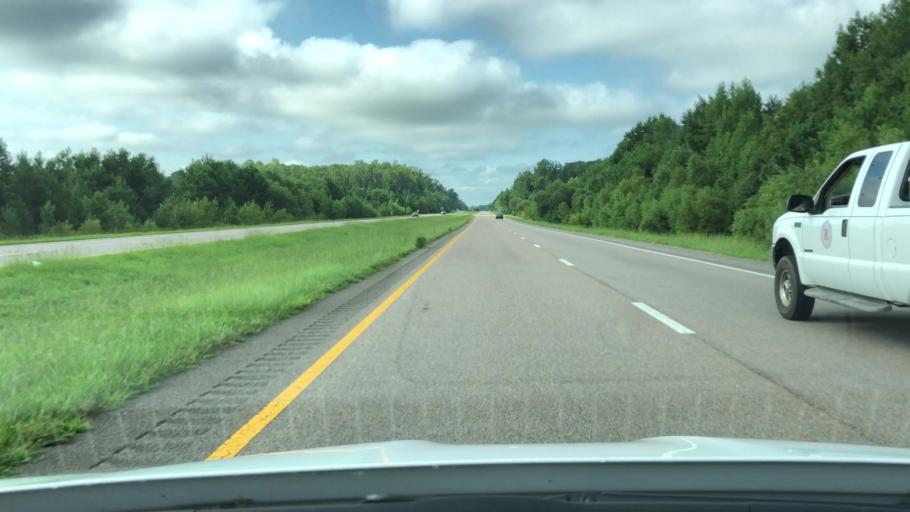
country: US
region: Virginia
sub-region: City of Portsmouth
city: Portsmouth Heights
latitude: 36.6411
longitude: -76.3620
